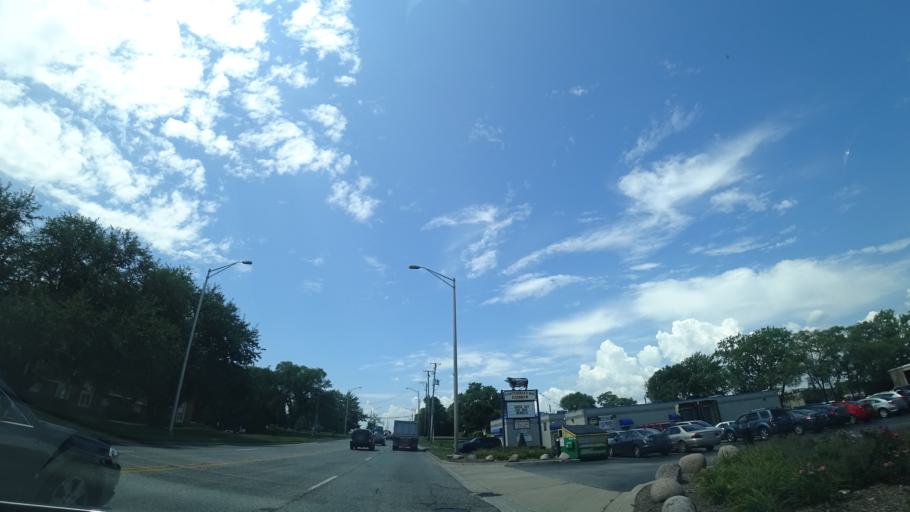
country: US
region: Illinois
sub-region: Cook County
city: Alsip
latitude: 41.6621
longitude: -87.7220
